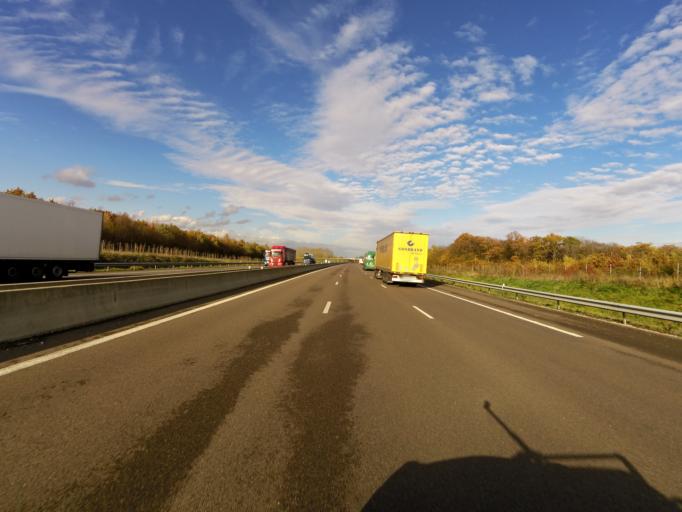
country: FR
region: Bourgogne
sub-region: Departement de la Cote-d'Or
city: Gevrey-Chambertin
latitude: 47.2057
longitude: 4.9976
